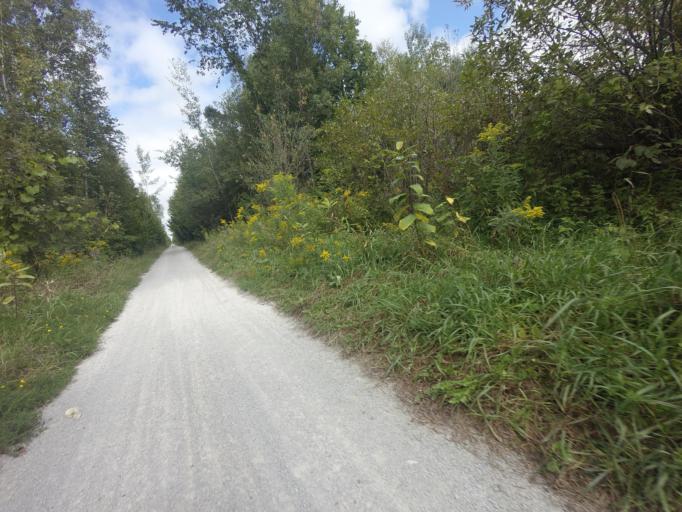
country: CA
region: Ontario
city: Uxbridge
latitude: 44.1659
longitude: -79.0786
